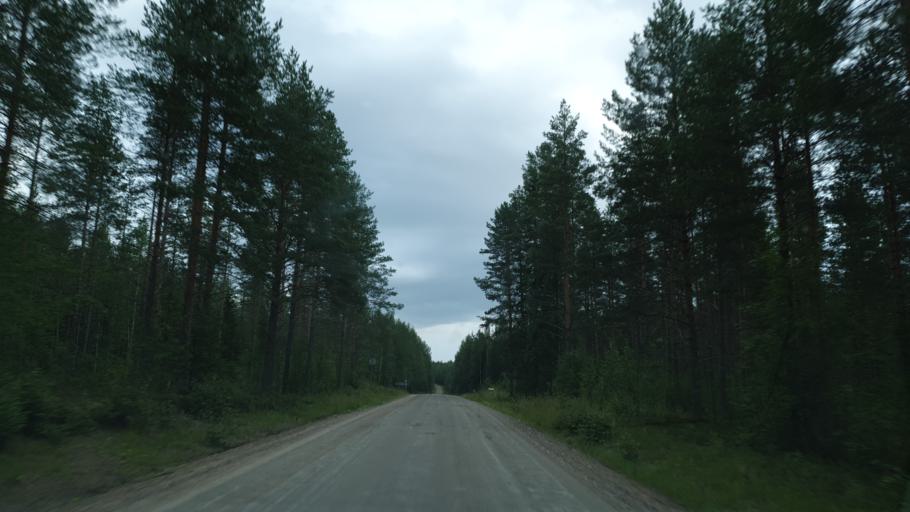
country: FI
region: Kainuu
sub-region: Kehys-Kainuu
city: Kuhmo
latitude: 64.1938
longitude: 29.3710
